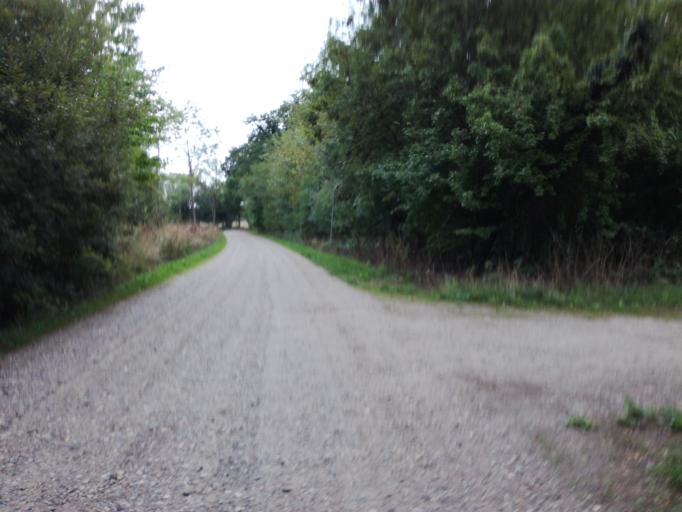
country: DK
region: South Denmark
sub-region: Fredericia Kommune
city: Fredericia
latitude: 55.6006
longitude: 9.7811
